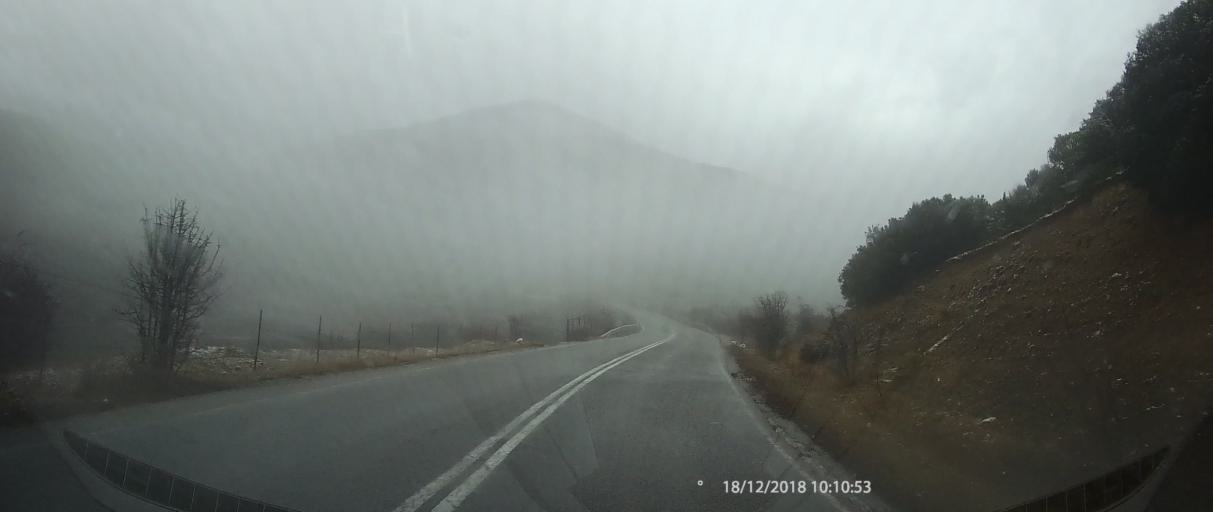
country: GR
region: Thessaly
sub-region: Nomos Larisis
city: Livadi
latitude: 40.0904
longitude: 22.2097
